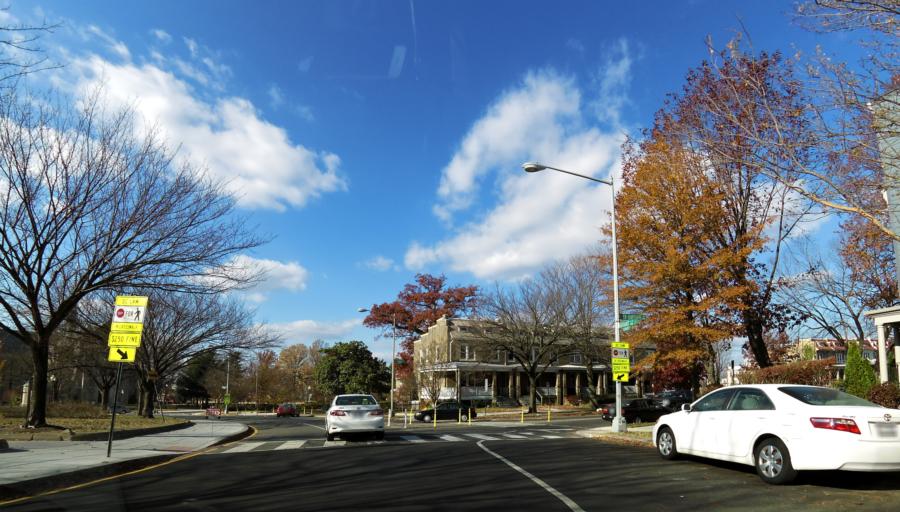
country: US
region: Maryland
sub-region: Prince George's County
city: Chillum
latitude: 38.9434
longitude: -77.0187
